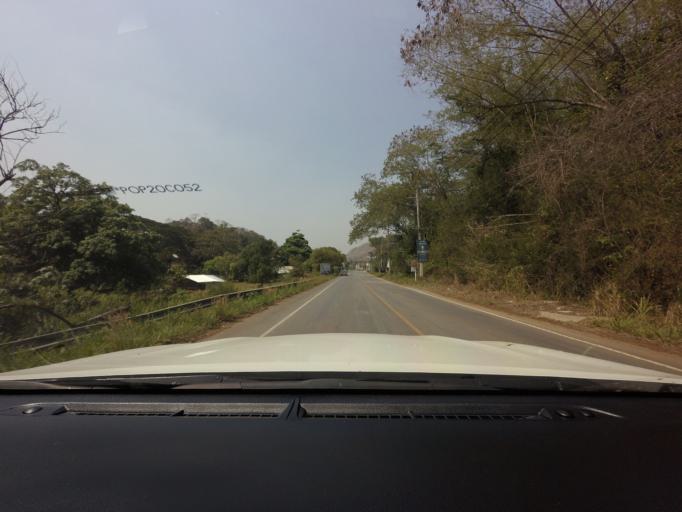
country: TH
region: Sara Buri
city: Muak Lek
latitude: 14.5405
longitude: 101.3415
